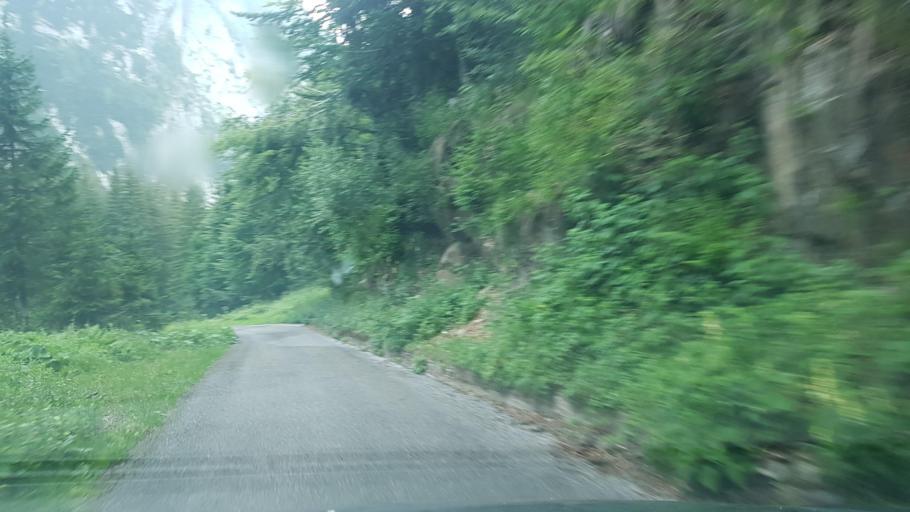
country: IT
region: Friuli Venezia Giulia
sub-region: Provincia di Udine
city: Paularo
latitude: 46.5754
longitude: 13.1444
